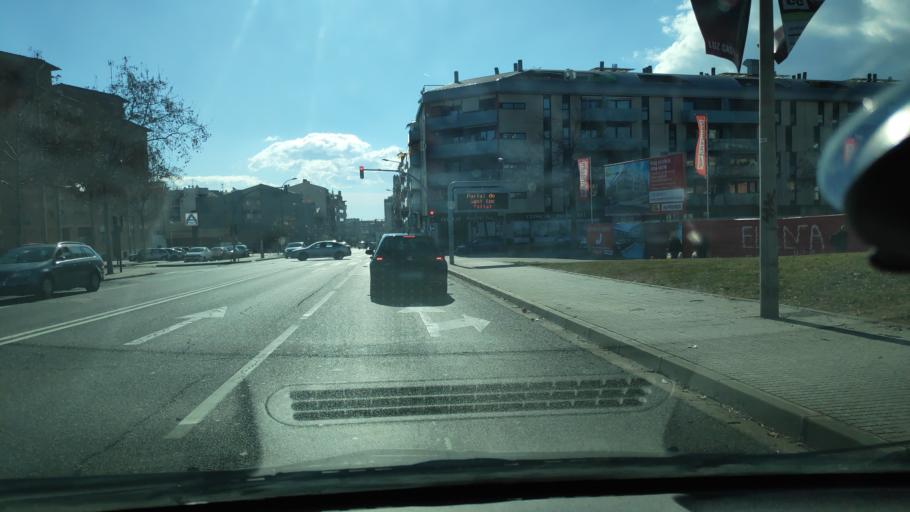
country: ES
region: Catalonia
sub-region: Provincia de Barcelona
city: Terrassa
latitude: 41.5781
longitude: 2.0176
